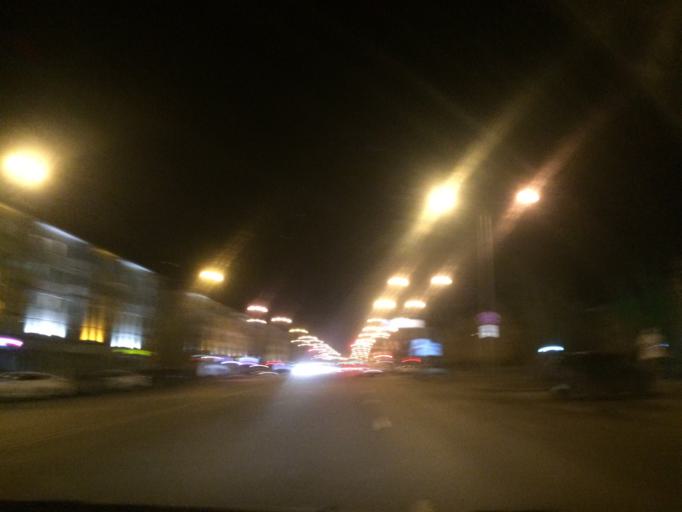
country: KZ
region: Astana Qalasy
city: Astana
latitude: 51.1864
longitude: 71.4082
